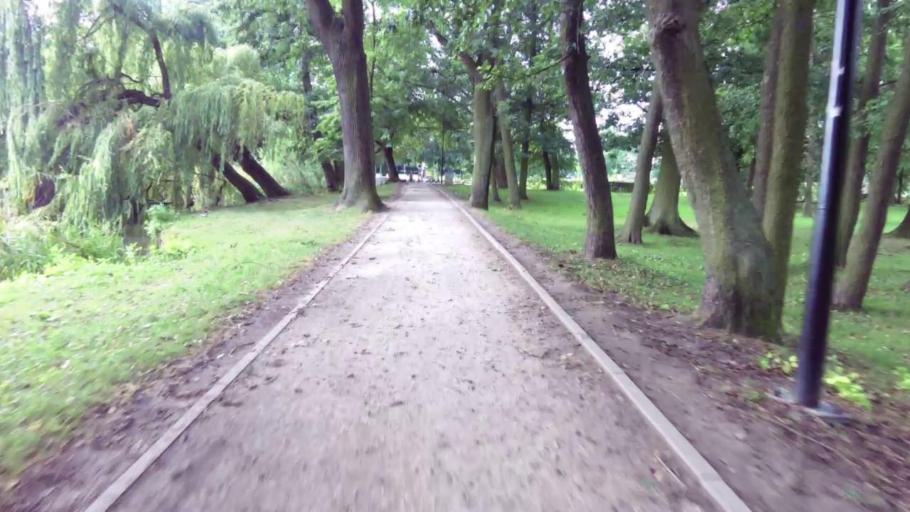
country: PL
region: West Pomeranian Voivodeship
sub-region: Powiat choszczenski
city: Choszczno
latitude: 53.1641
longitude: 15.4178
